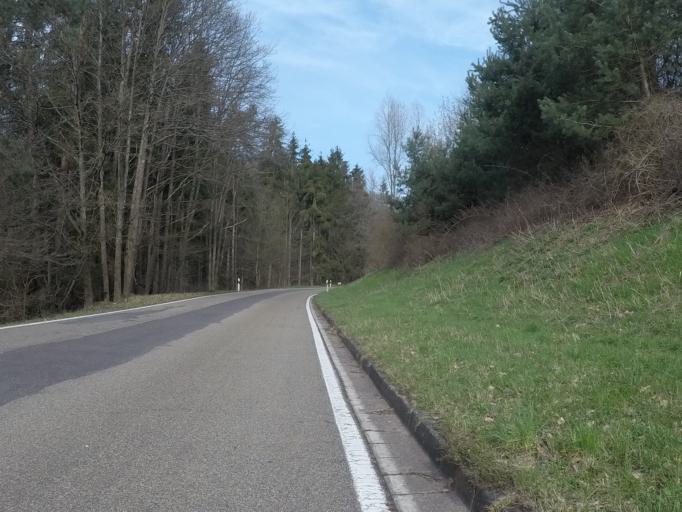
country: DE
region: Rheinland-Pfalz
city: Spirkelbach
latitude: 49.1835
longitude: 7.8823
